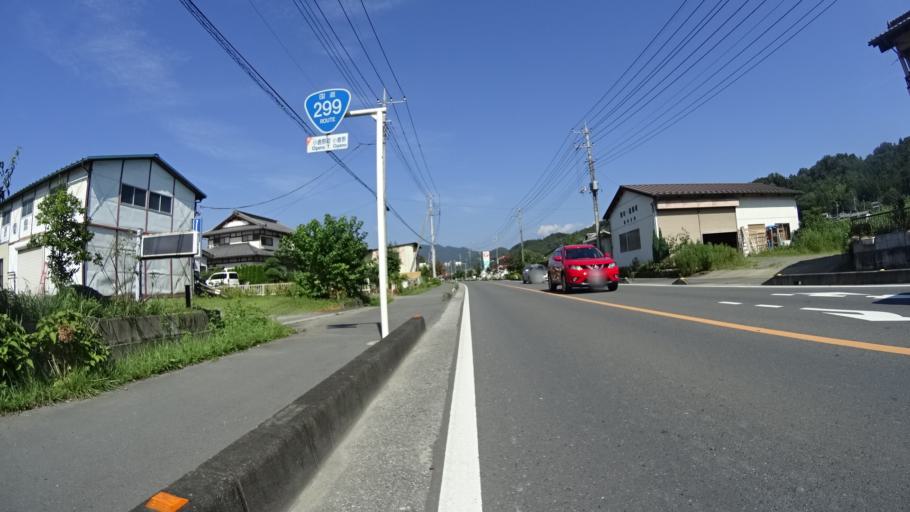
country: JP
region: Saitama
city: Chichibu
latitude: 36.0222
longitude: 139.0060
